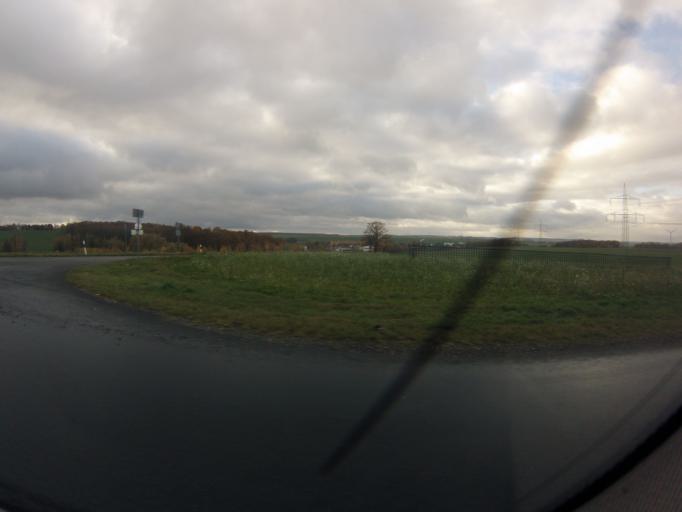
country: DE
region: Thuringia
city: Thonhausen
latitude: 50.8493
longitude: 12.3286
